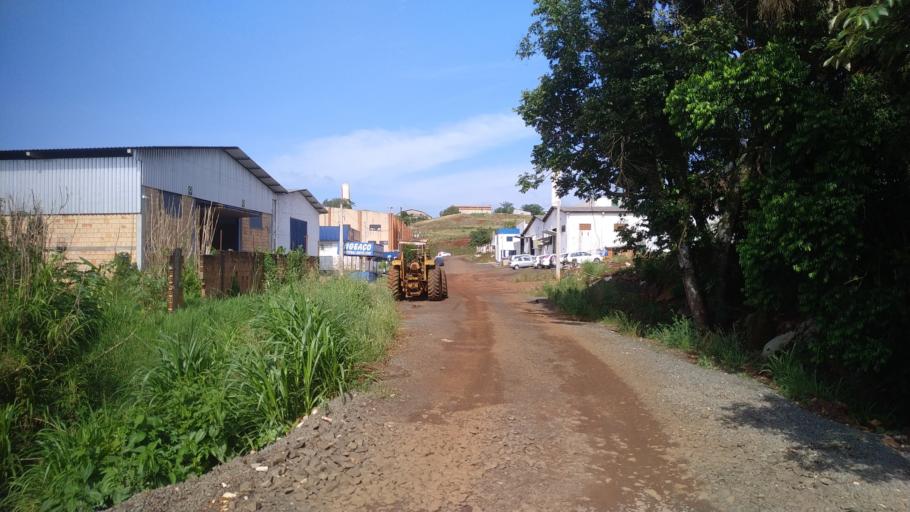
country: BR
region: Santa Catarina
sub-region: Chapeco
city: Chapeco
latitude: -27.0705
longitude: -52.6217
